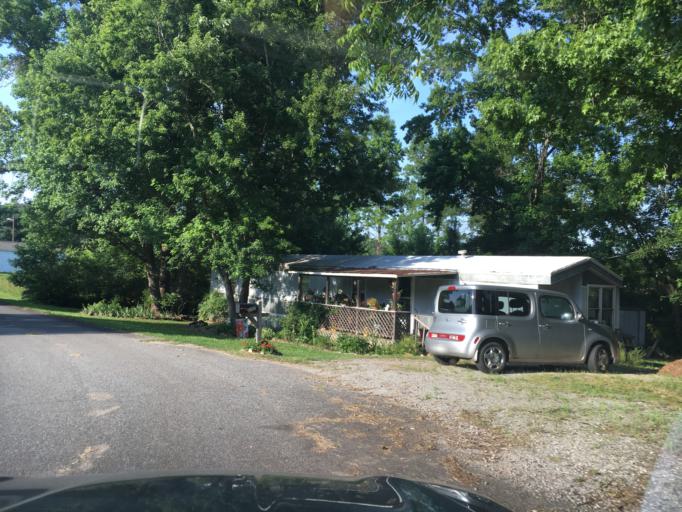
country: US
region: South Carolina
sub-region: Spartanburg County
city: Duncan
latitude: 34.8591
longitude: -82.1091
